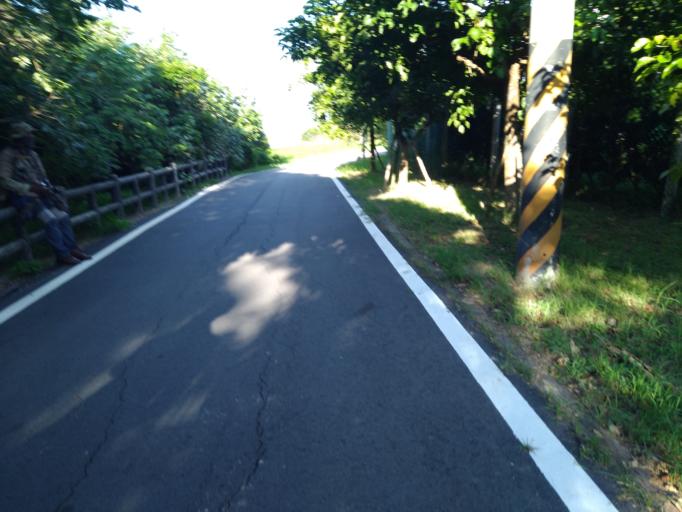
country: TW
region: Taiwan
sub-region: Hsinchu
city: Hsinchu
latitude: 24.7675
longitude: 120.9287
